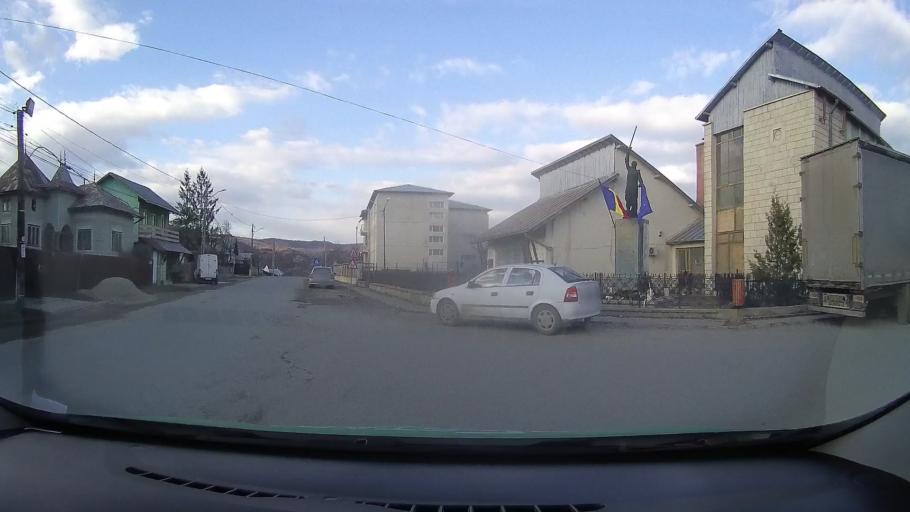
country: RO
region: Dambovita
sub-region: Comuna Ocnita
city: Ocnita
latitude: 44.9882
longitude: 25.5542
